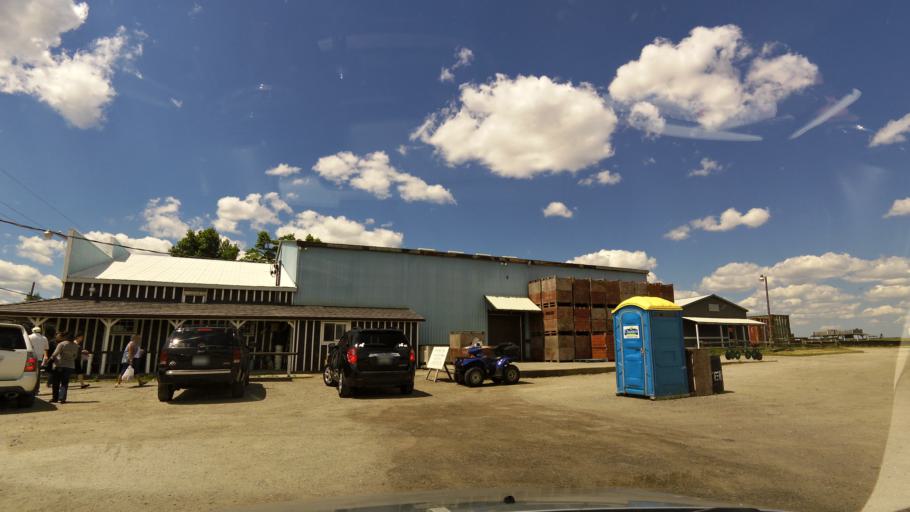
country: CA
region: Ontario
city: Brampton
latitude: 43.6293
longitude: -79.8016
